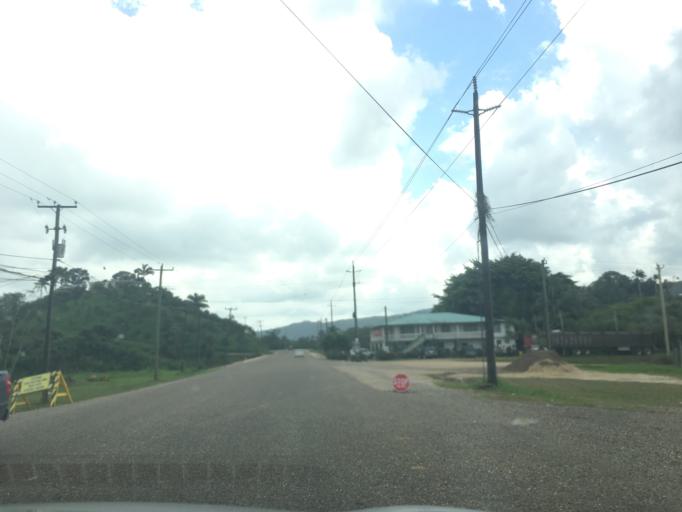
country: BZ
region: Stann Creek
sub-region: Dangriga
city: Dangriga
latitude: 16.9903
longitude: -88.4021
